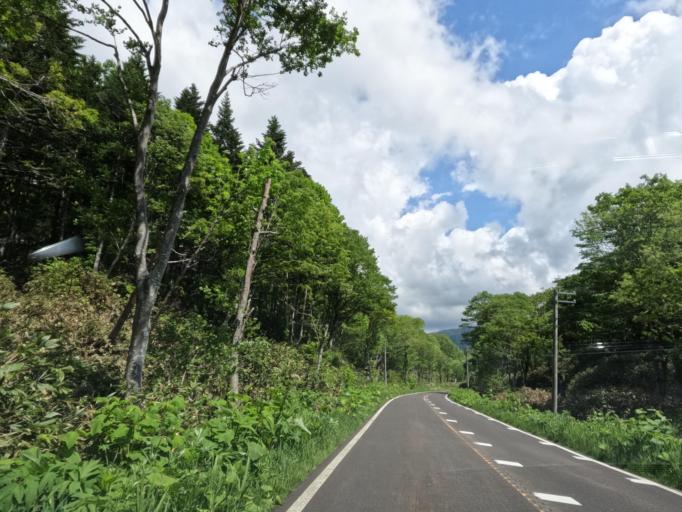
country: JP
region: Hokkaido
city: Takikawa
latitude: 43.5444
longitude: 141.6298
